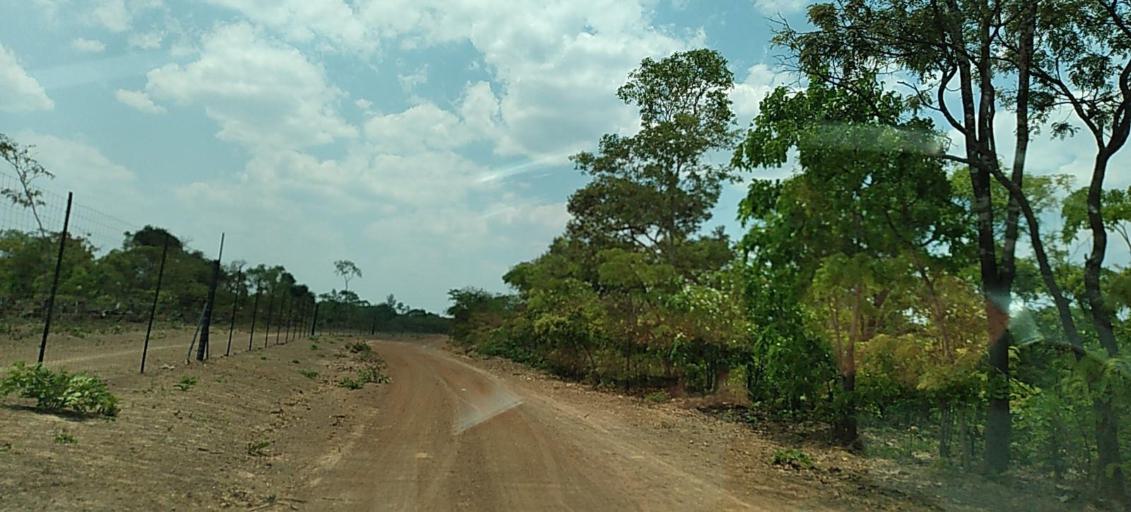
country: ZM
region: Copperbelt
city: Chililabombwe
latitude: -12.5254
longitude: 27.6264
